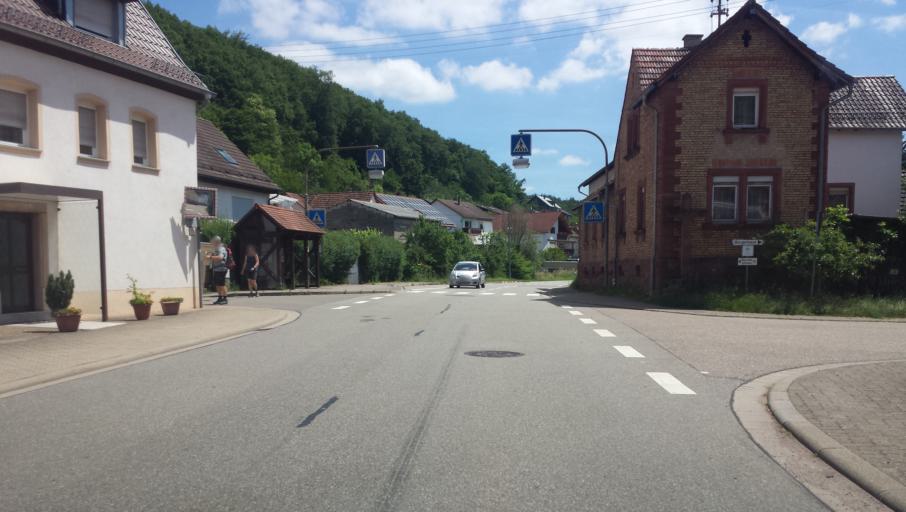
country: DE
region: Rheinland-Pfalz
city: Waldrohrbach
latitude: 49.1704
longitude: 7.9659
